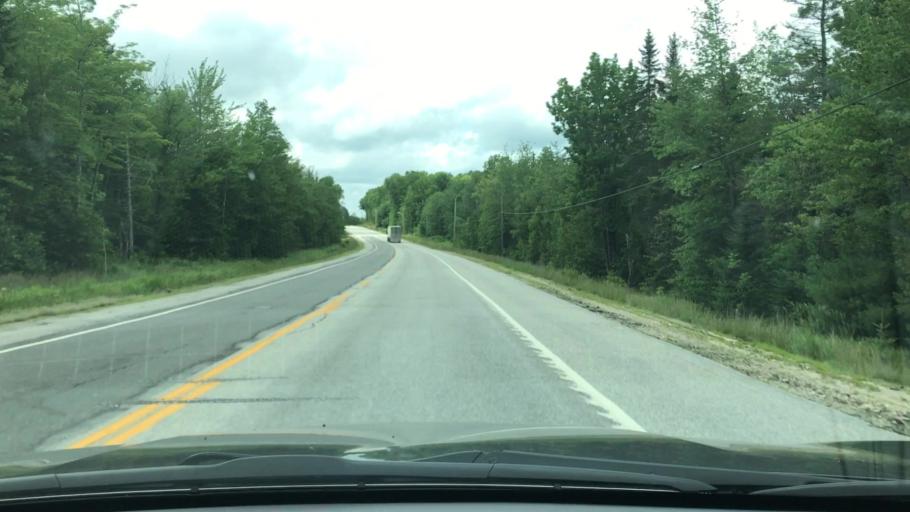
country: US
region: Maine
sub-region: Oxford County
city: West Paris
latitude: 44.3658
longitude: -70.5917
